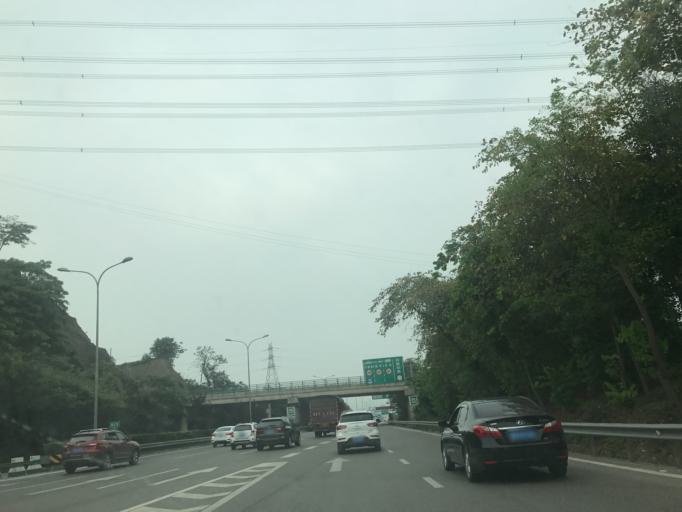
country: CN
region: Chongqing Shi
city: Cuntan
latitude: 29.6130
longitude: 106.5605
